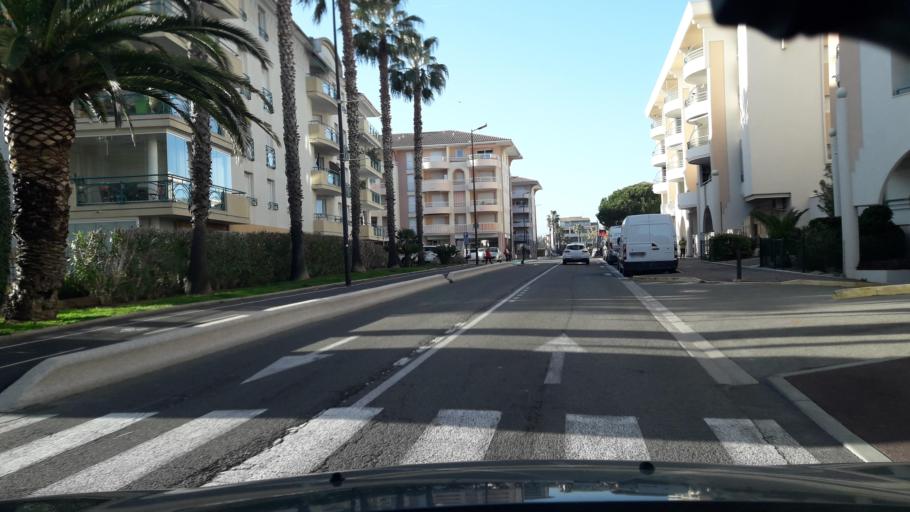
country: FR
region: Provence-Alpes-Cote d'Azur
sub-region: Departement du Var
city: Frejus
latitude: 43.4207
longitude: 6.7462
